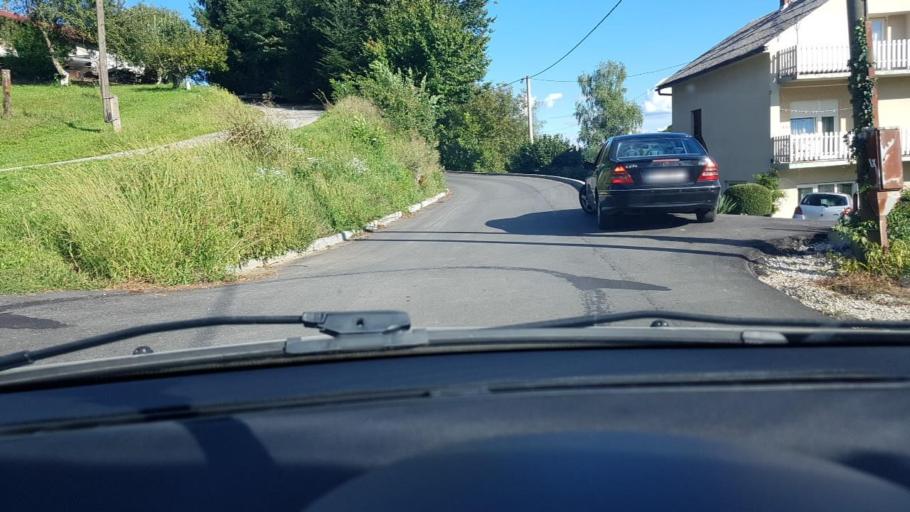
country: HR
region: Krapinsko-Zagorska
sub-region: Grad Krapina
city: Krapina
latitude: 46.1278
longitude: 15.8449
